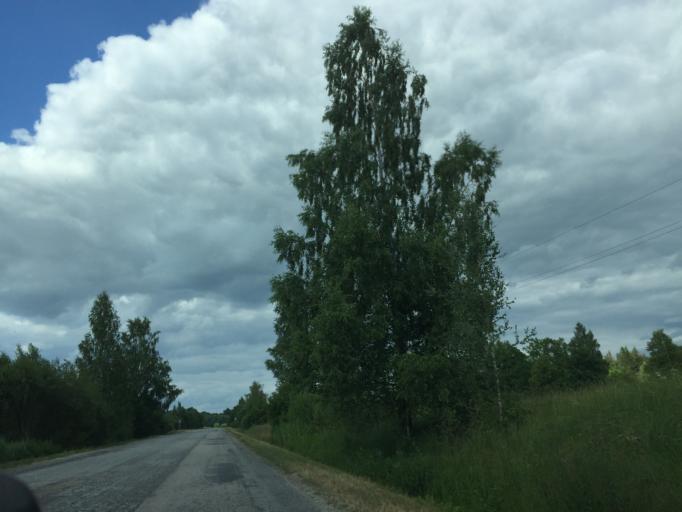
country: LV
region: Skriveri
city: Skriveri
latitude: 56.8206
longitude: 25.1203
